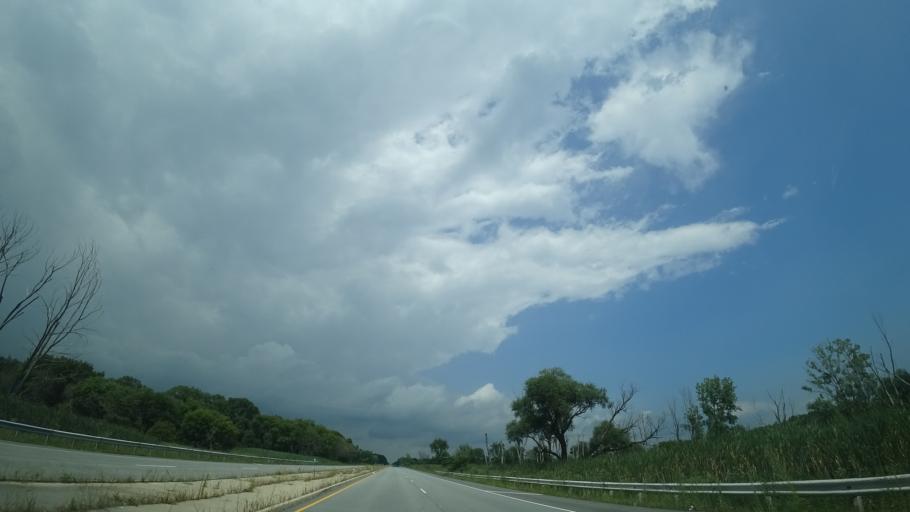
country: US
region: Illinois
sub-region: Cook County
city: Matteson
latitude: 41.5315
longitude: -87.7325
